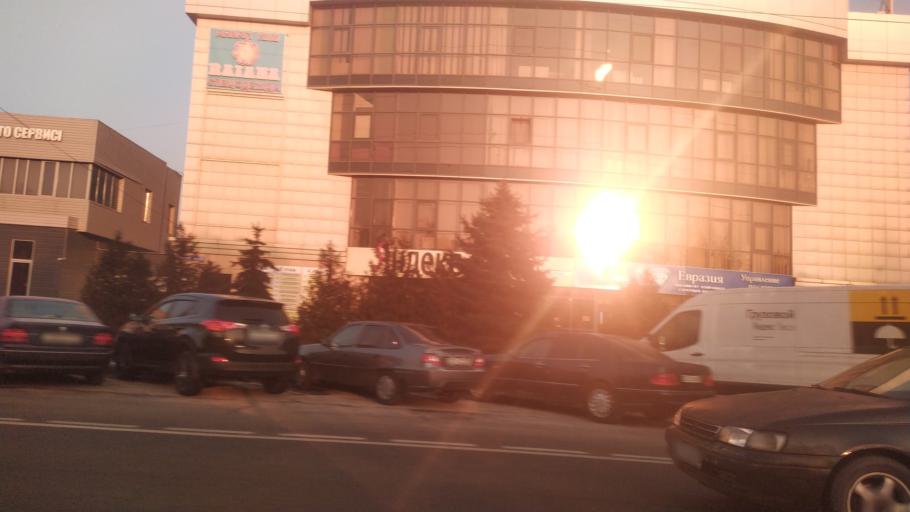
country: KZ
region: Almaty Qalasy
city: Almaty
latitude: 43.2630
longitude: 76.8973
